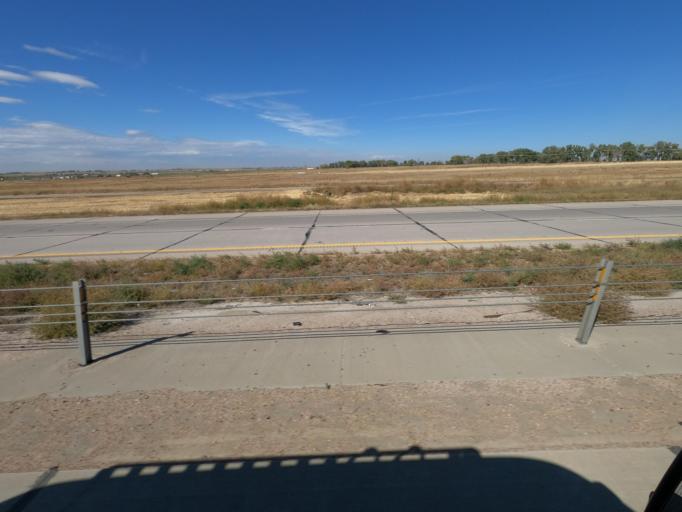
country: US
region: Colorado
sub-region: Weld County
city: Hudson
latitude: 40.0789
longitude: -104.6410
